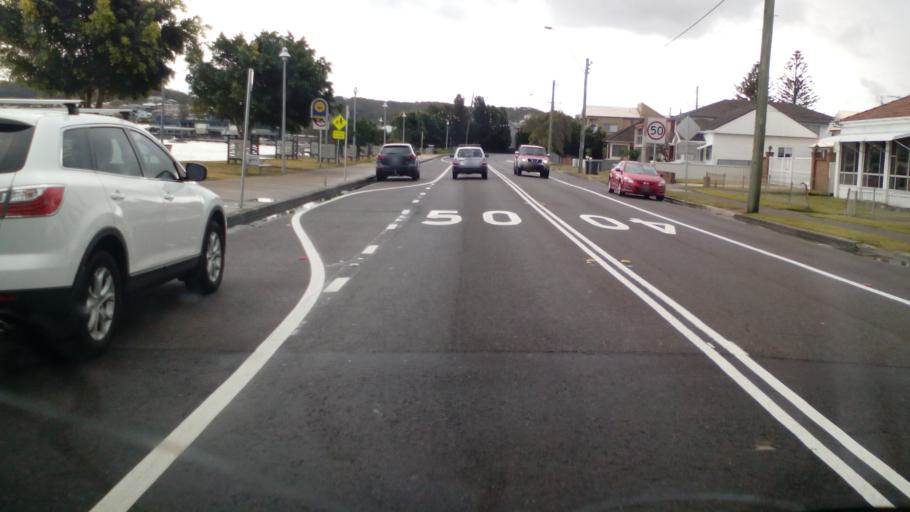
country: AU
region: New South Wales
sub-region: Lake Macquarie Shire
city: Belmont
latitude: -33.0338
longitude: 151.6565
